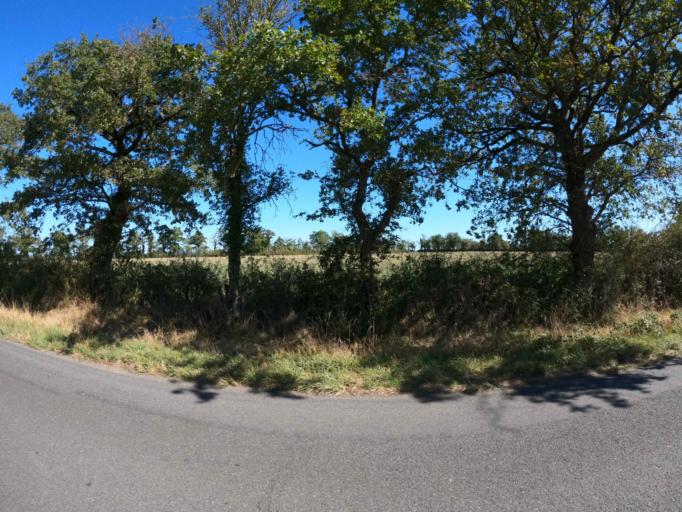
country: FR
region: Poitou-Charentes
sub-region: Departement de la Vienne
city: Lathus-Saint-Remy
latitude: 46.2984
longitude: 0.9954
